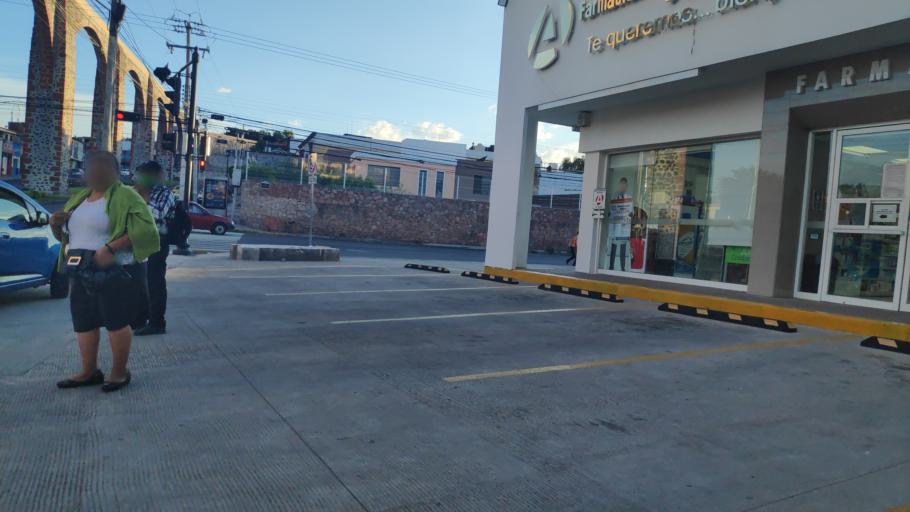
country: MX
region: Queretaro
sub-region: Queretaro
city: Santiago de Queretaro
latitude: 20.5926
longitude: -100.3780
